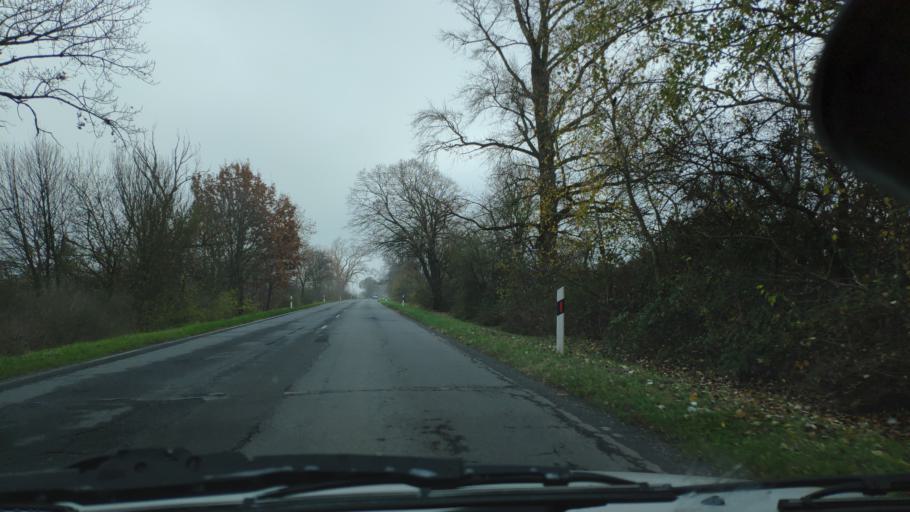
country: HU
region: Zala
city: Zalakomar
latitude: 46.5643
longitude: 17.2615
